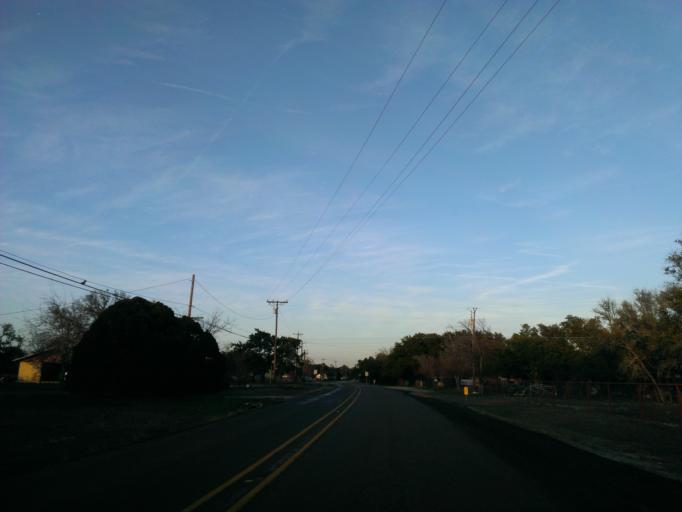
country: US
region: Texas
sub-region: Burnet County
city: Bertram
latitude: 30.7387
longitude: -98.0652
